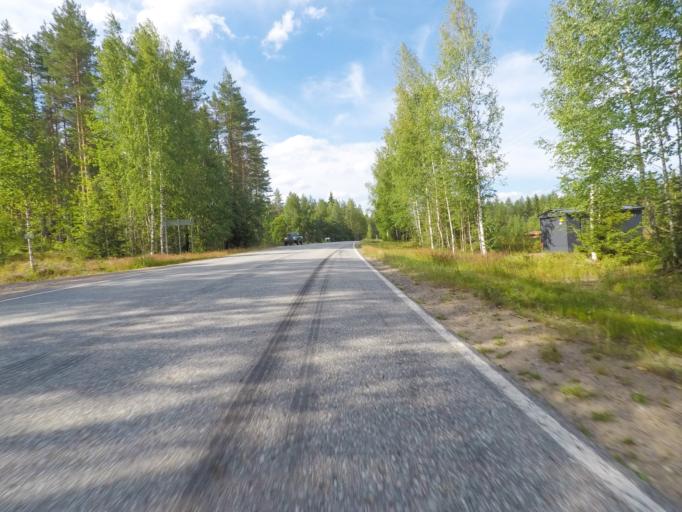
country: FI
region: Southern Savonia
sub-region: Savonlinna
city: Sulkava
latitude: 61.7212
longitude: 28.2060
